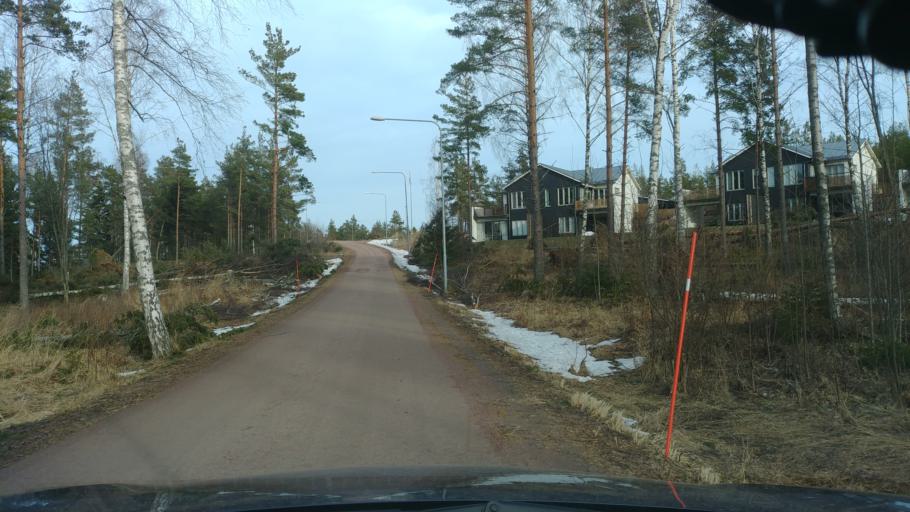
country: AX
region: Mariehamns stad
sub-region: Mariehamn
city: Mariehamn
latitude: 60.1010
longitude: 19.8864
